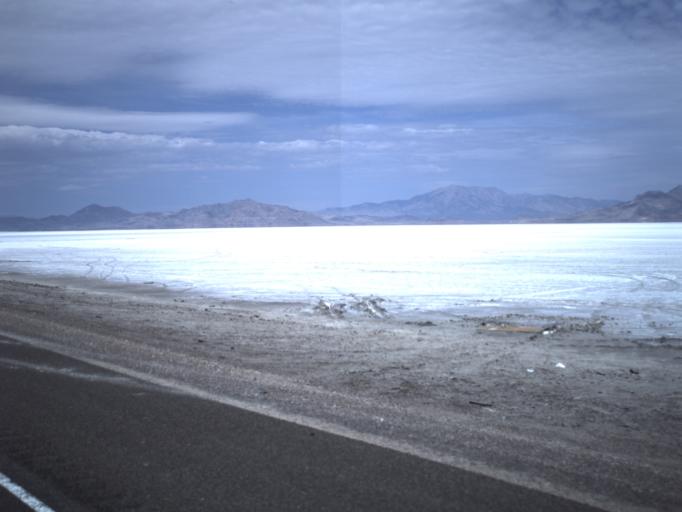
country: US
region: Utah
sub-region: Tooele County
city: Wendover
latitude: 40.7365
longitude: -113.7093
